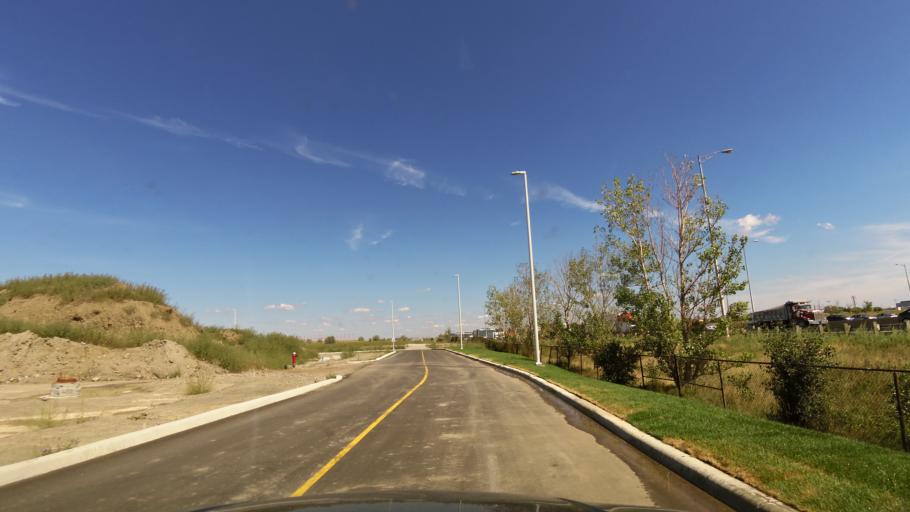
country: CA
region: Ontario
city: Etobicoke
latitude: 43.6510
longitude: -79.6325
